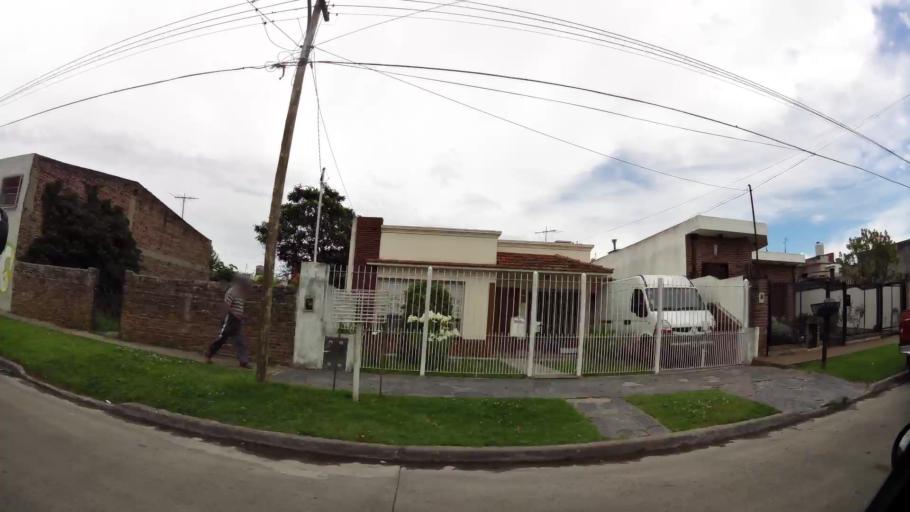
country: AR
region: Buenos Aires
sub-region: Partido de Quilmes
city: Quilmes
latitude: -34.7557
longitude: -58.2317
